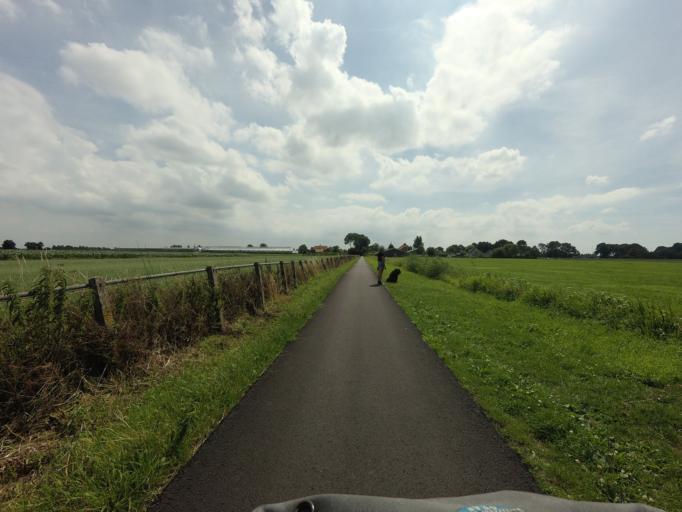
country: NL
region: Utrecht
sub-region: Gemeente De Ronde Venen
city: Mijdrecht
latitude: 52.1723
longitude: 4.8282
